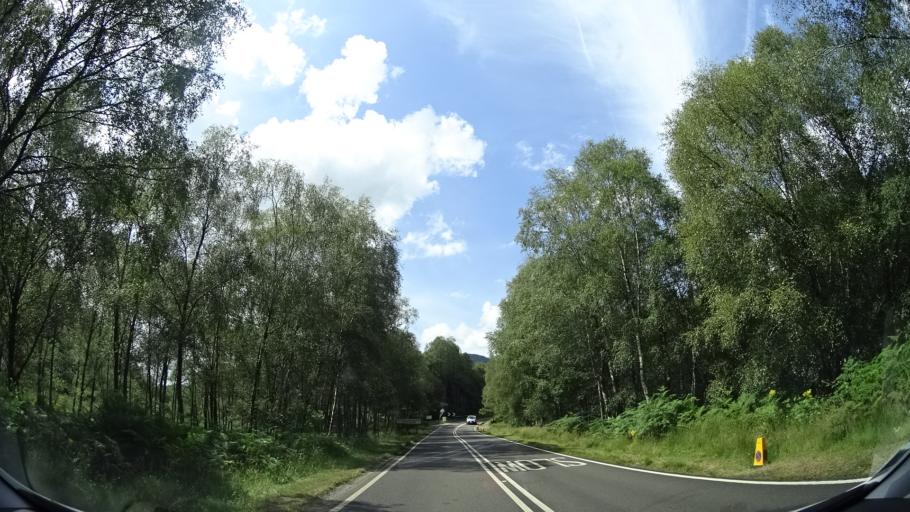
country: GB
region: Scotland
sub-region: Highland
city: Fort William
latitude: 56.8683
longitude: -5.4305
